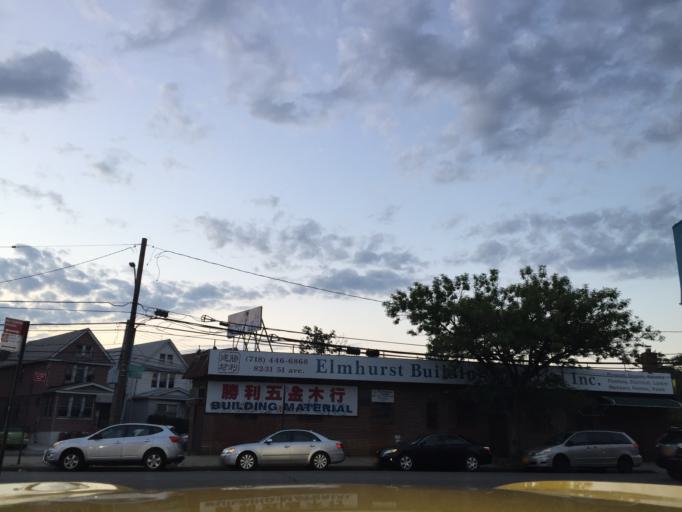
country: US
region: New York
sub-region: Queens County
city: Long Island City
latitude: 40.7379
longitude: -73.8809
